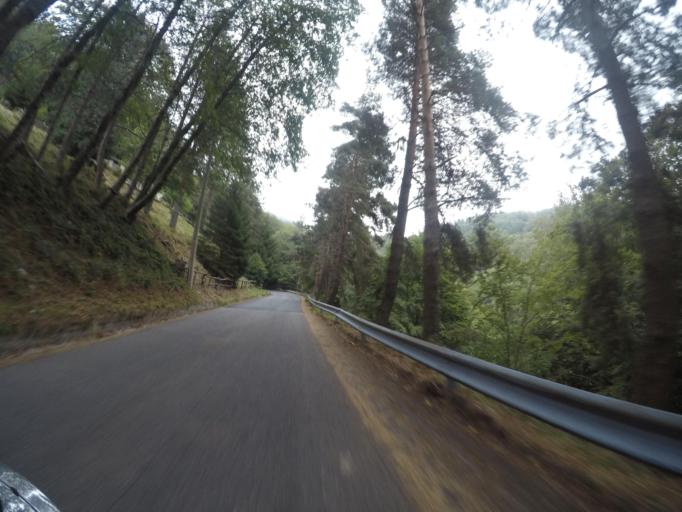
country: IT
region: Tuscany
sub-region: Provincia di Massa-Carrara
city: Carrara
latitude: 44.1179
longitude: 10.1186
